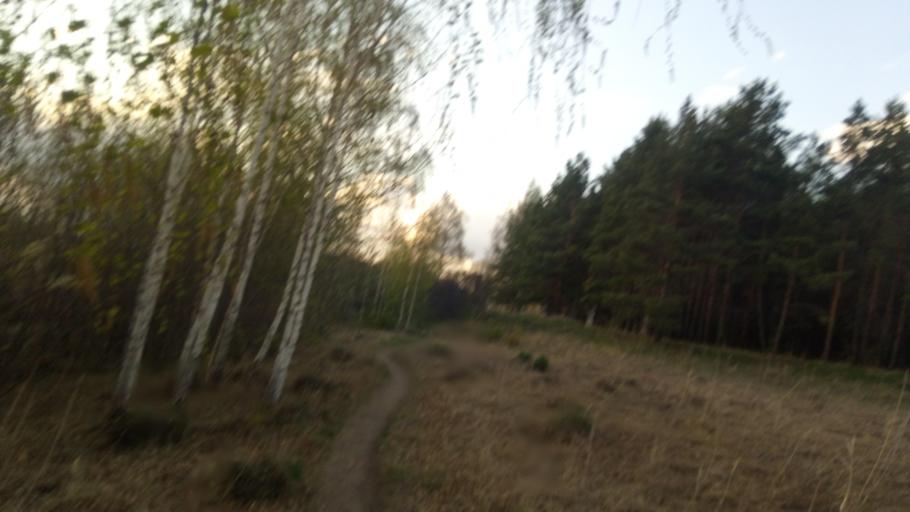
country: RU
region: Chelyabinsk
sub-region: Gorod Chelyabinsk
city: Chelyabinsk
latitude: 55.1618
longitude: 61.3129
